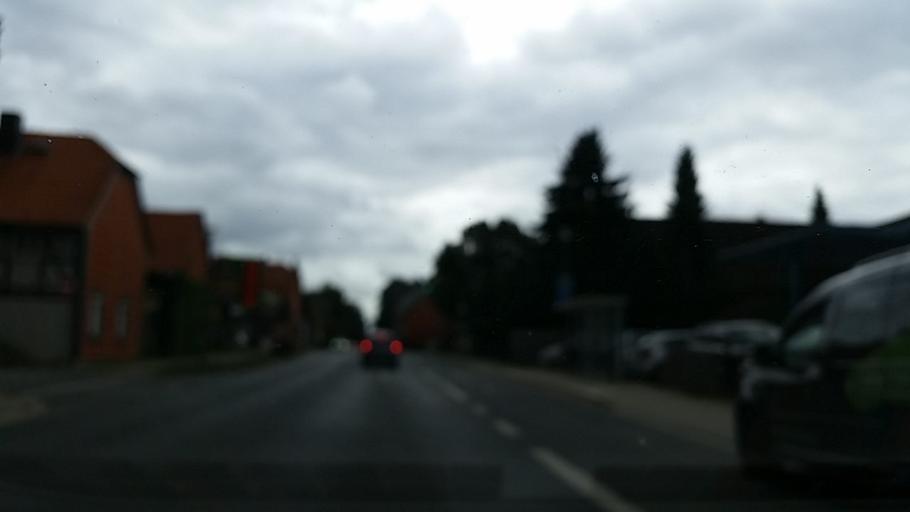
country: DE
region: Lower Saxony
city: Wolfenbuettel
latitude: 52.1428
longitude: 10.5481
